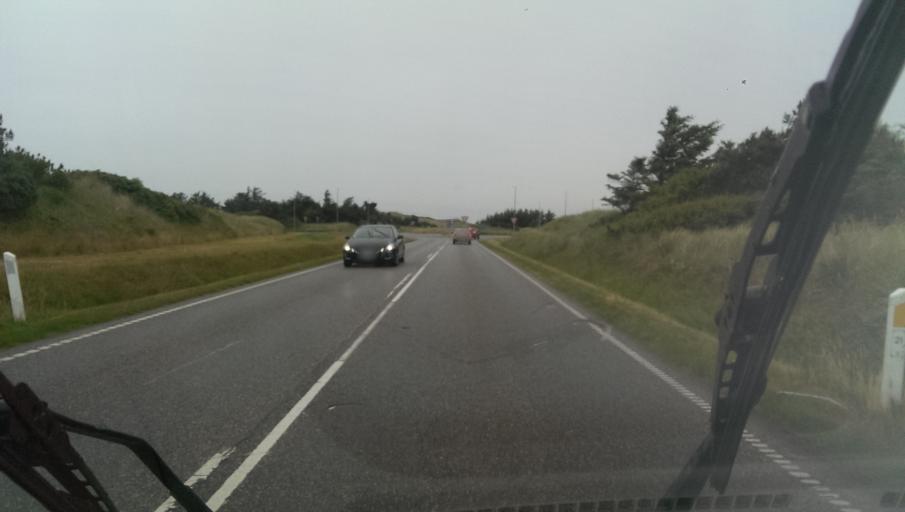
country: DK
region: Central Jutland
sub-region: Ringkobing-Skjern Kommune
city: Hvide Sande
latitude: 56.0196
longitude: 8.1238
